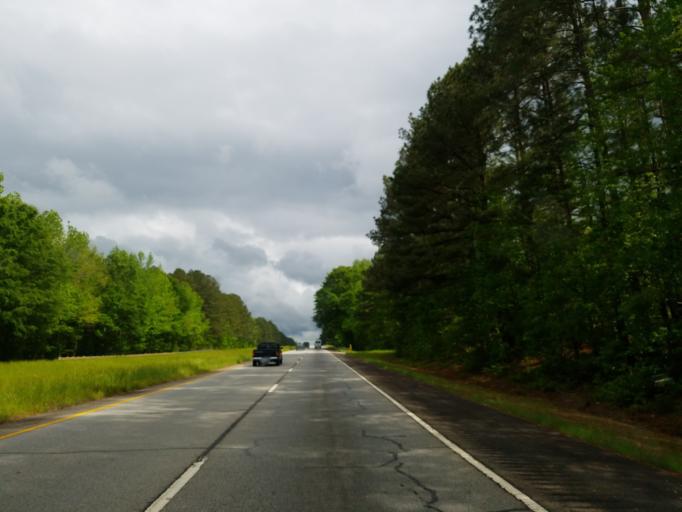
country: US
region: Georgia
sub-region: Lamar County
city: Barnesville
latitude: 33.1328
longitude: -84.2287
